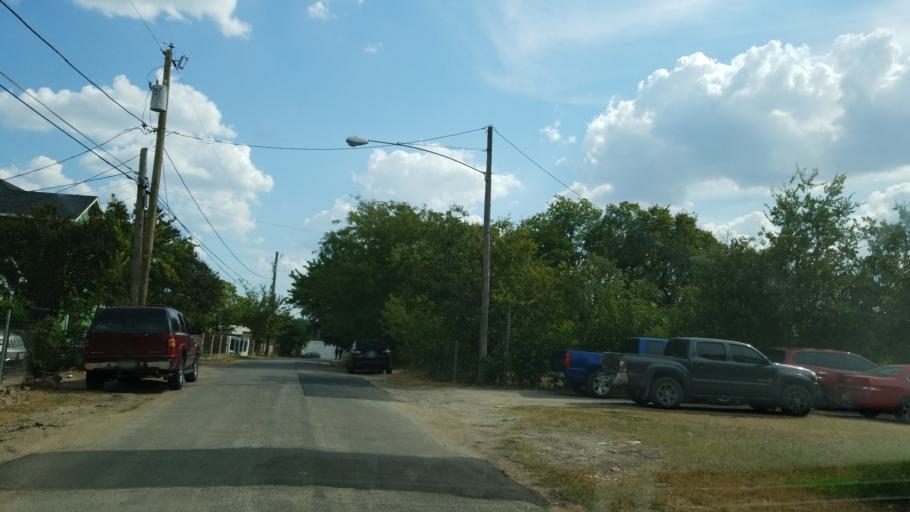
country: US
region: Texas
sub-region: Dallas County
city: Dallas
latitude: 32.7668
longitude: -96.8458
